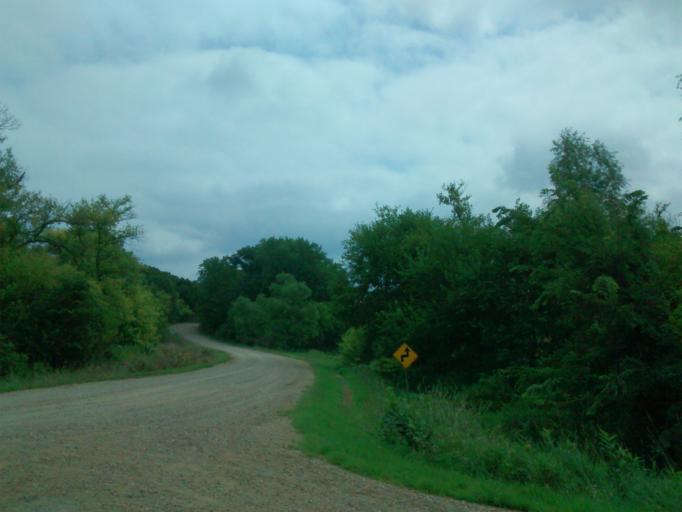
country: US
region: Iowa
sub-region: Woodbury County
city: Moville
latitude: 42.4737
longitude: -96.0770
